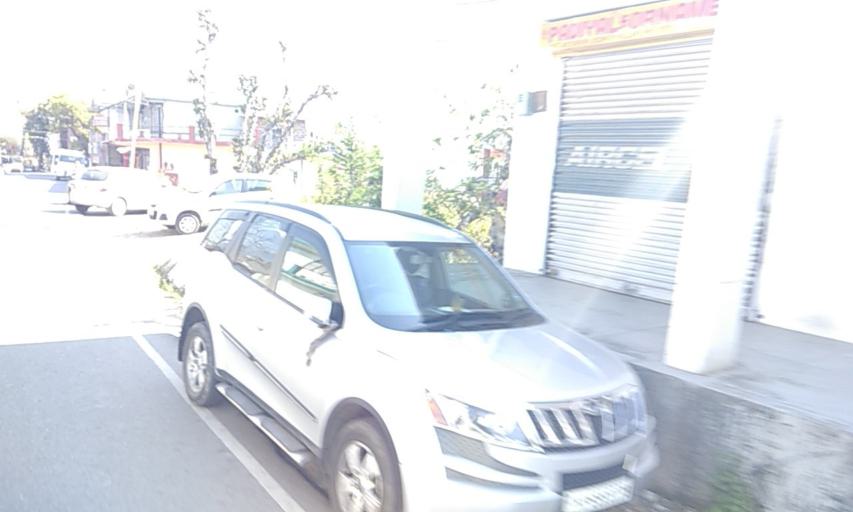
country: IN
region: Himachal Pradesh
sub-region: Kangra
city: Dharmsala
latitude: 32.1859
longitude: 76.3660
